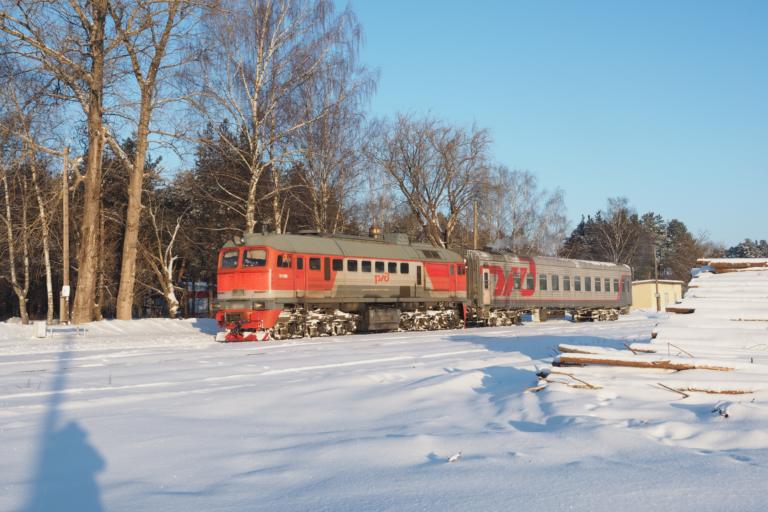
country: RU
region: Tverskaya
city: Ves'yegonsk
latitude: 58.6535
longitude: 37.2637
